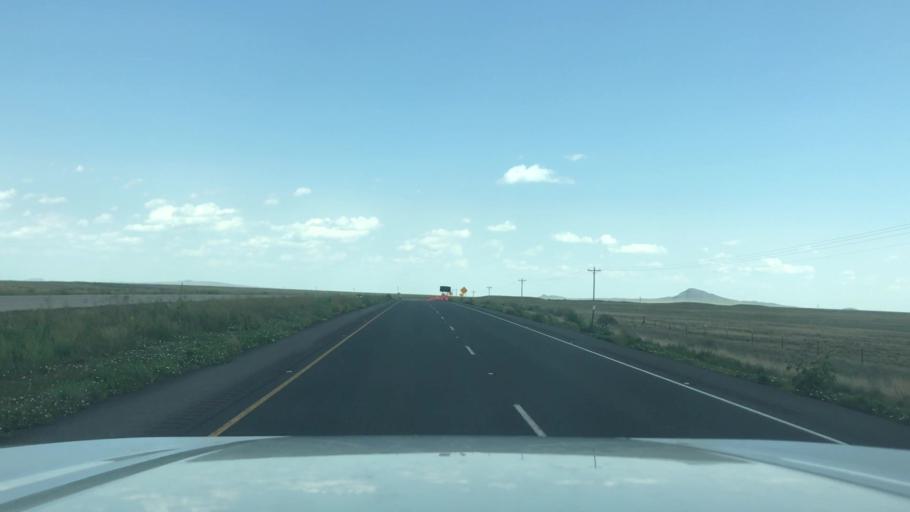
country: US
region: New Mexico
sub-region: Union County
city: Clayton
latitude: 36.6180
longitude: -103.6911
